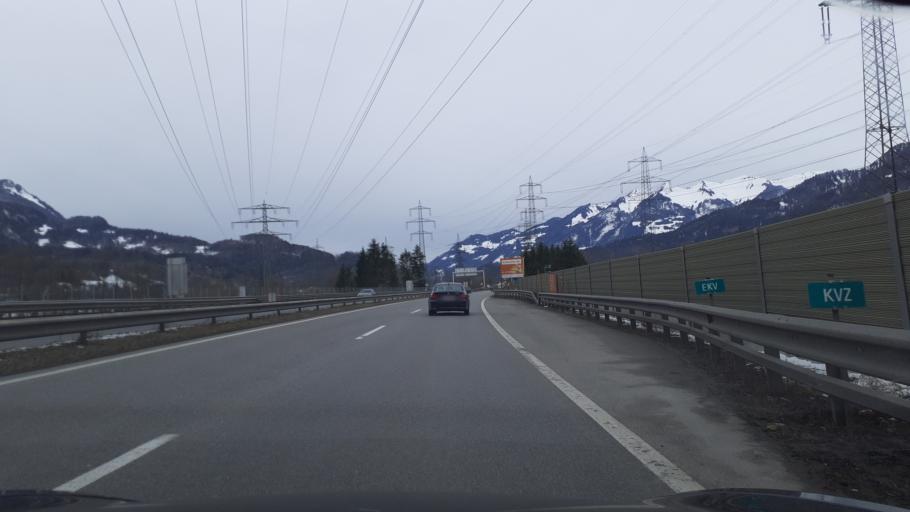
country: AT
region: Vorarlberg
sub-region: Politischer Bezirk Bludenz
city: Bludenz
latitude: 47.1392
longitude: 9.8266
